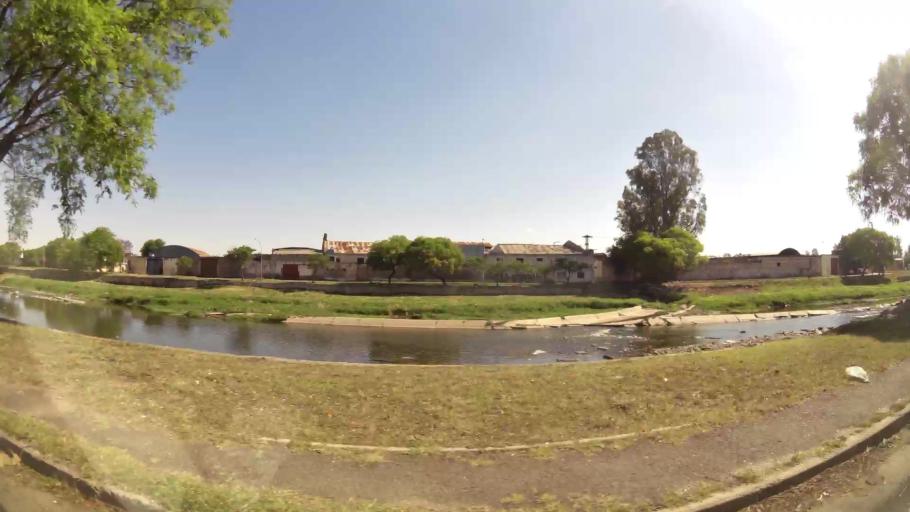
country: AR
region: Cordoba
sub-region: Departamento de Capital
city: Cordoba
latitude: -31.4172
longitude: -64.1529
